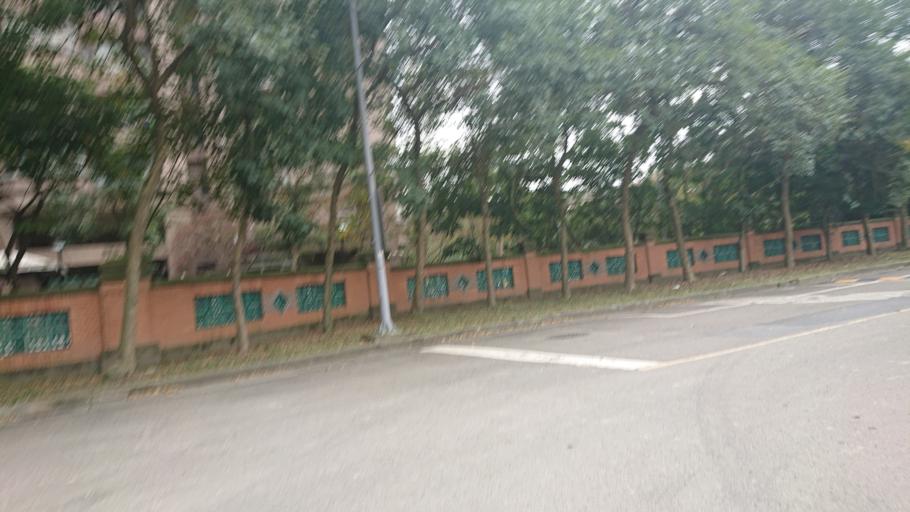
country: TW
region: Taiwan
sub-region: Taoyuan
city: Taoyuan
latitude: 24.9423
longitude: 121.3702
